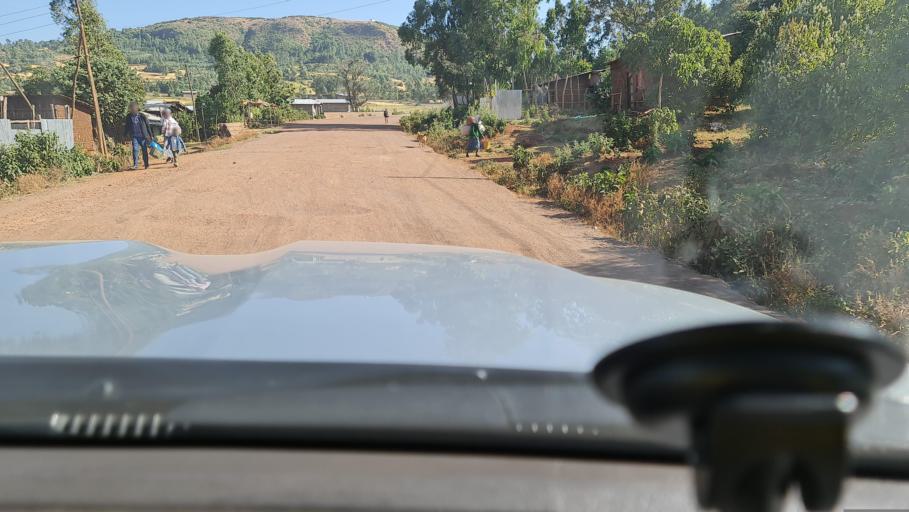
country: ET
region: Oromiya
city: Waliso
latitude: 8.6108
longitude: 37.9230
